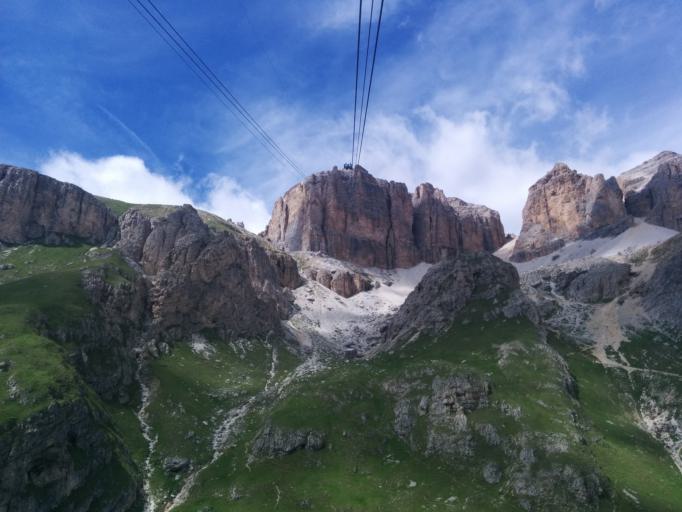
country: IT
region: Trentino-Alto Adige
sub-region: Provincia di Trento
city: Canazei
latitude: 46.4908
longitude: 11.8102
